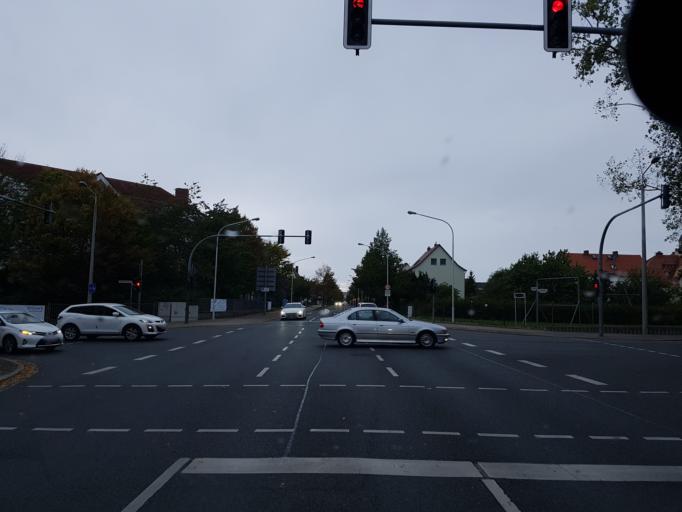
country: DE
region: Saxony
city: Riesa
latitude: 51.3001
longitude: 13.3024
